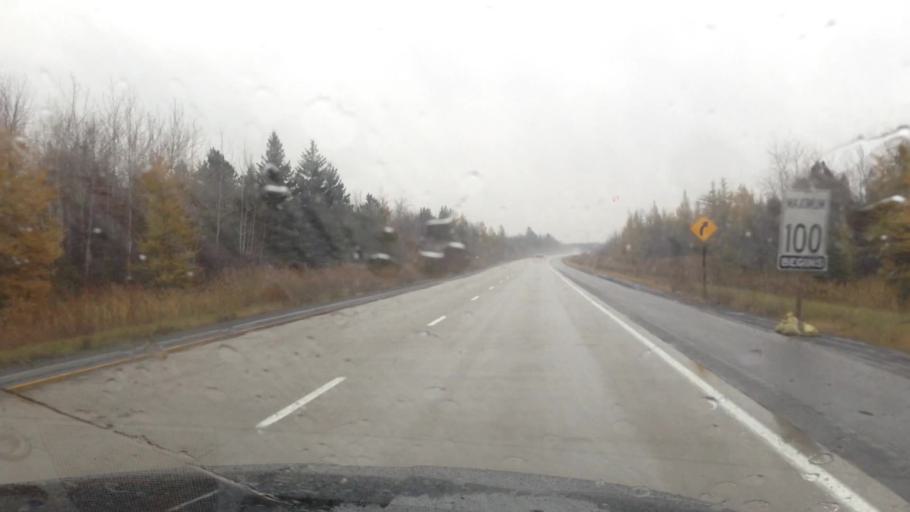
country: CA
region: Ontario
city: Hawkesbury
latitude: 45.4867
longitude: -74.6303
